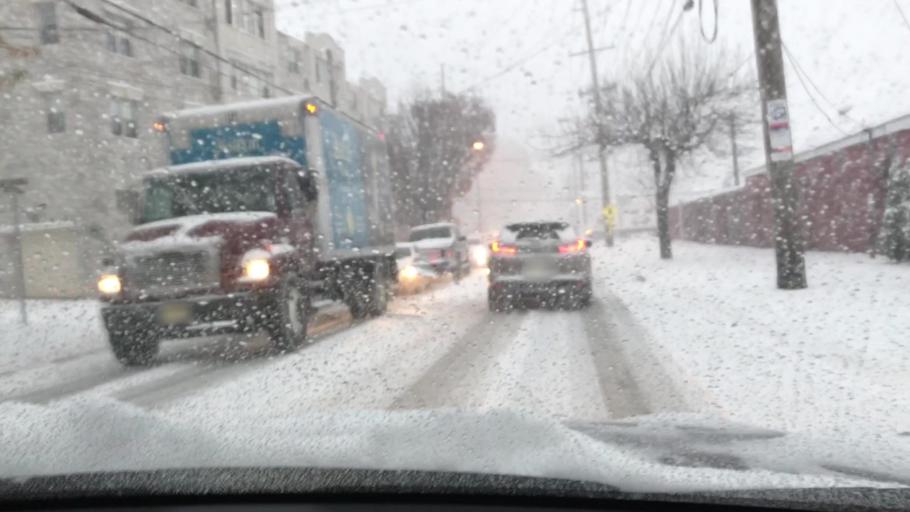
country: US
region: New Jersey
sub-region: Bergen County
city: East Rutherford
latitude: 40.8269
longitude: -74.0988
